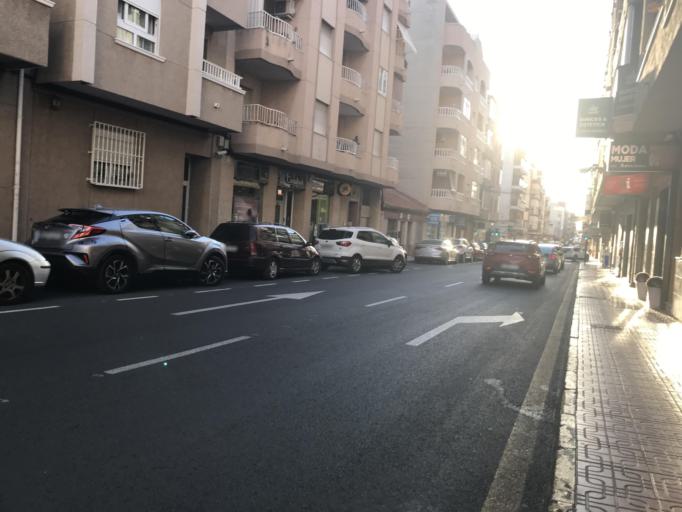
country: ES
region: Valencia
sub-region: Provincia de Alicante
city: Torrevieja
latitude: 37.9795
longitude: -0.6777
